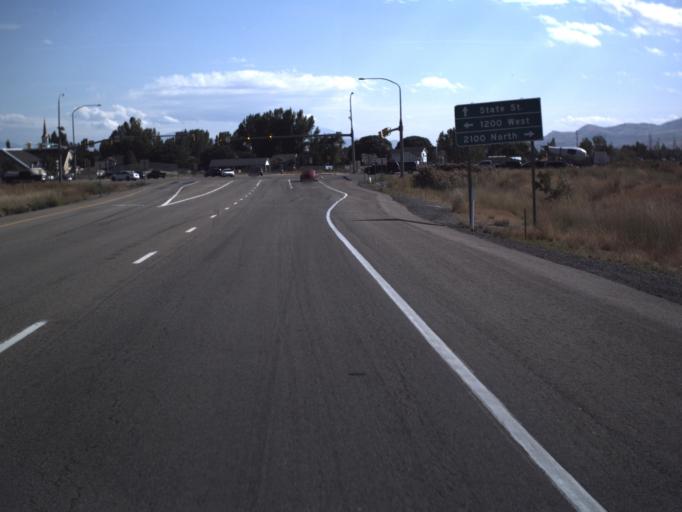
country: US
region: Utah
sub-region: Utah County
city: Lehi
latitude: 40.4147
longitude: -111.8731
